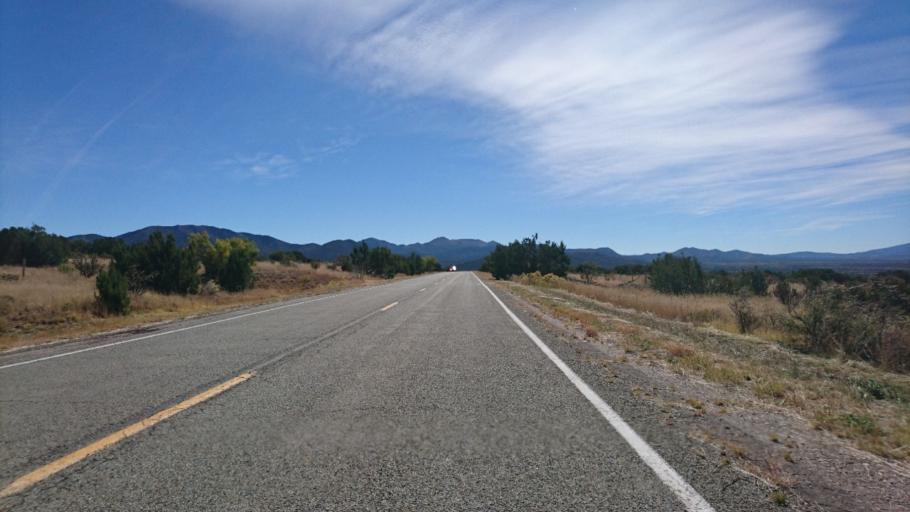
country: US
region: New Mexico
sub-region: Bernalillo County
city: Sandia Knolls
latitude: 35.3028
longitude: -106.2157
